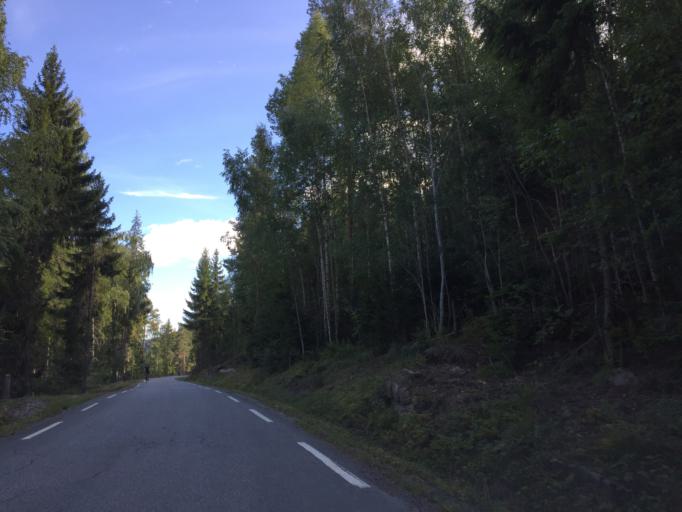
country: NO
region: Buskerud
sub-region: Ovre Eiker
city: Hokksund
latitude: 59.6489
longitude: 9.9191
